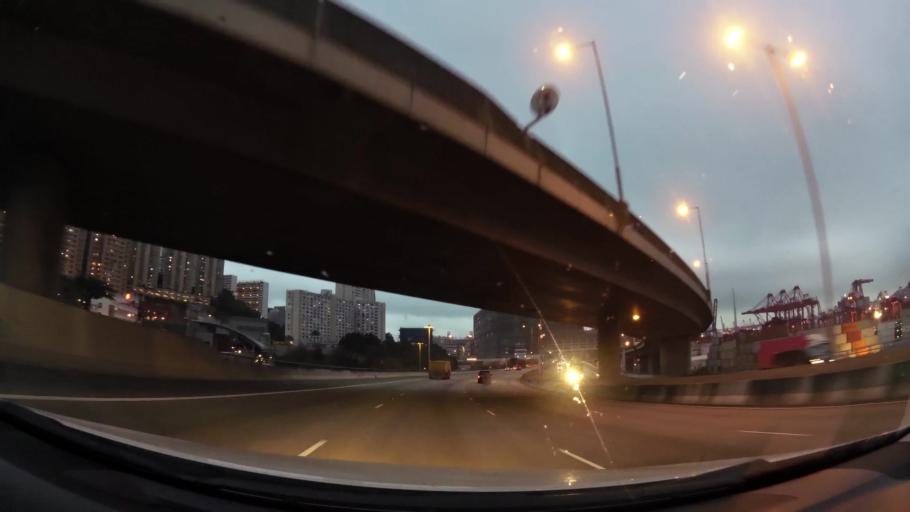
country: HK
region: Tsuen Wan
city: Tsuen Wan
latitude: 22.3501
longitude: 114.1245
